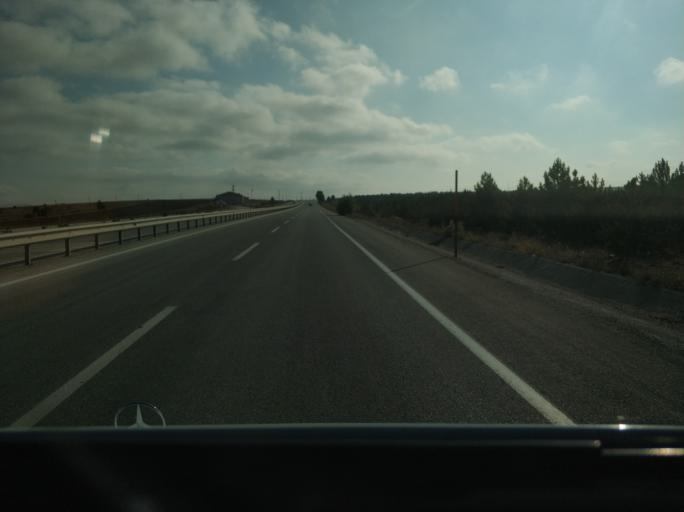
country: TR
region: Sivas
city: Yavu
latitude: 39.8321
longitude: 36.3902
